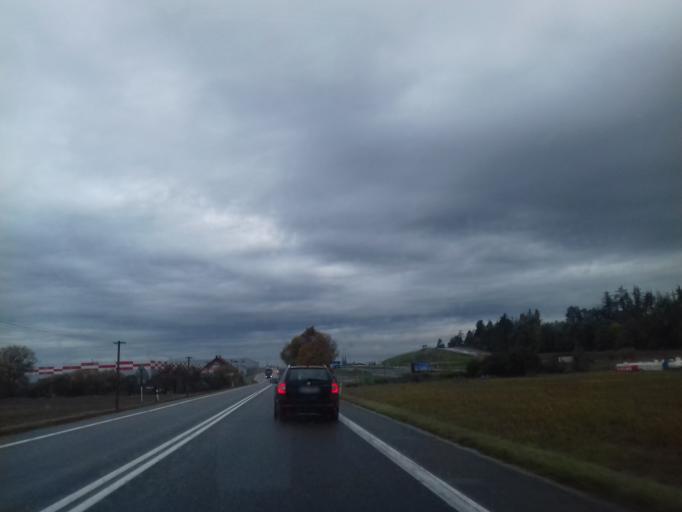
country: CZ
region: Pardubicky
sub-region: Okres Pardubice
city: Vysoke Myto
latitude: 49.9327
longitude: 16.1750
